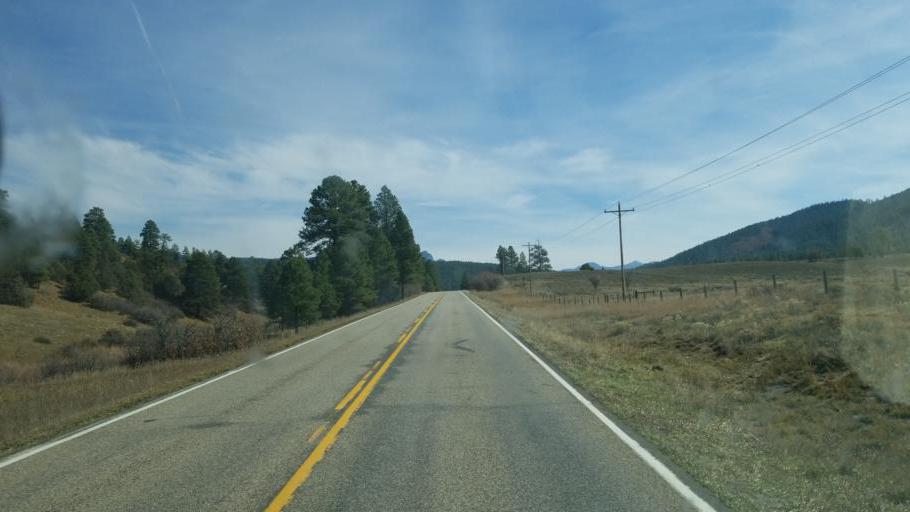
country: US
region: New Mexico
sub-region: Rio Arriba County
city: Dulce
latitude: 37.0800
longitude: -106.8830
